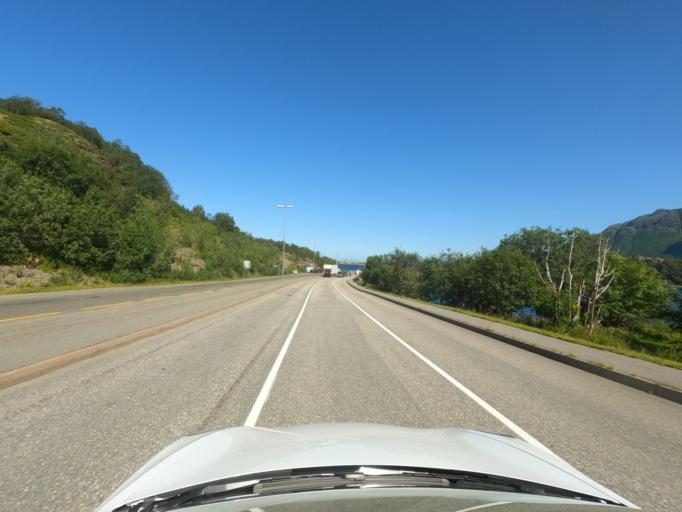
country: NO
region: Nordland
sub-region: Hadsel
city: Melbu
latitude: 68.4299
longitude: 14.8213
